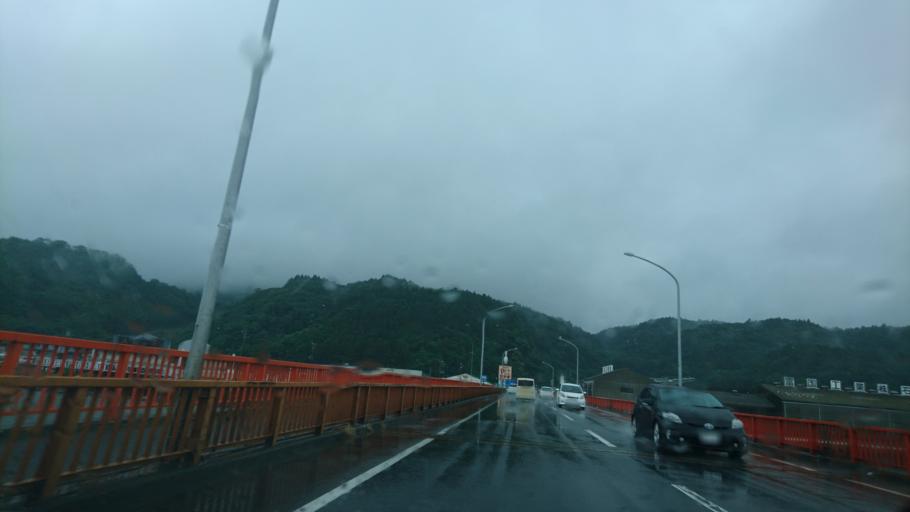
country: JP
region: Miyagi
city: Ishinomaki
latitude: 38.4380
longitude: 141.3168
